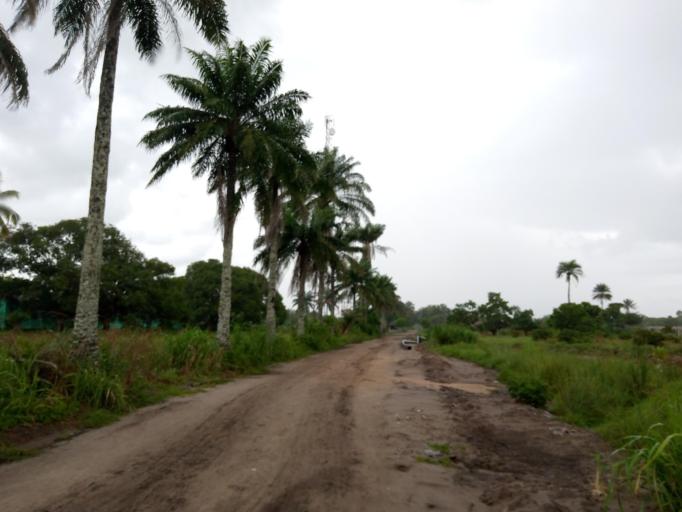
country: SL
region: Southern Province
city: Bonthe
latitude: 7.5274
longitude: -12.5122
